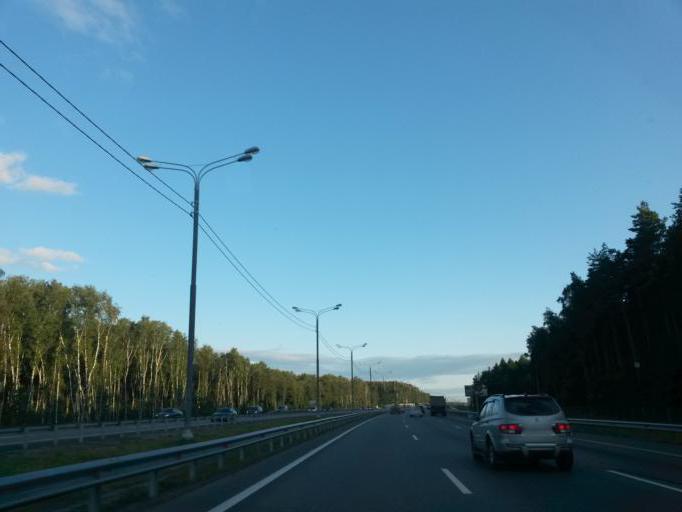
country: RU
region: Moskovskaya
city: Vostryakovo
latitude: 55.4392
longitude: 37.7989
